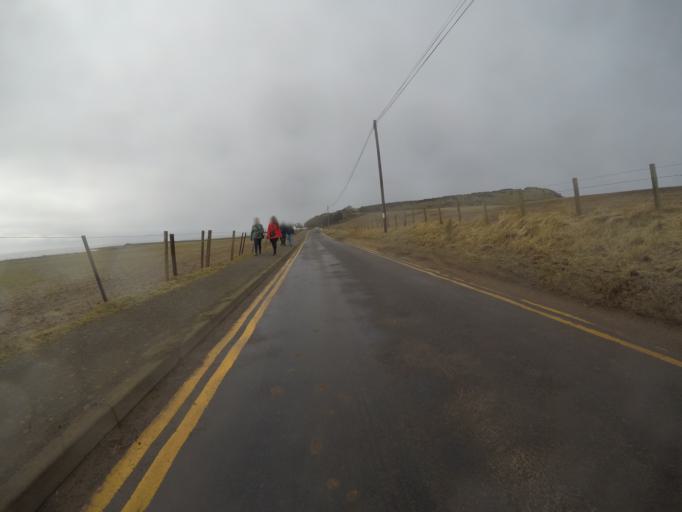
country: GB
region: Scotland
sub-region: North Ayrshire
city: West Kilbride
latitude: 55.6979
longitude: -4.8938
